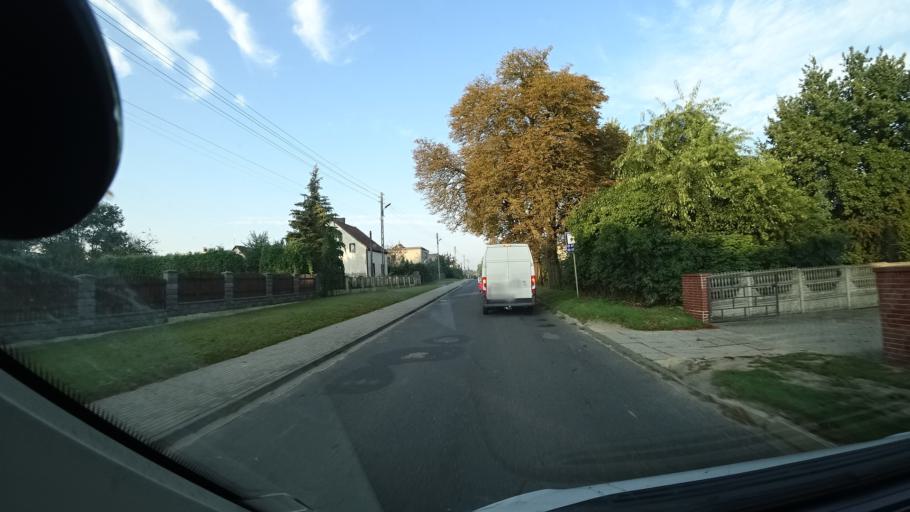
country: PL
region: Opole Voivodeship
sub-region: Powiat kedzierzynsko-kozielski
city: Slawiecice
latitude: 50.3755
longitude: 18.3315
